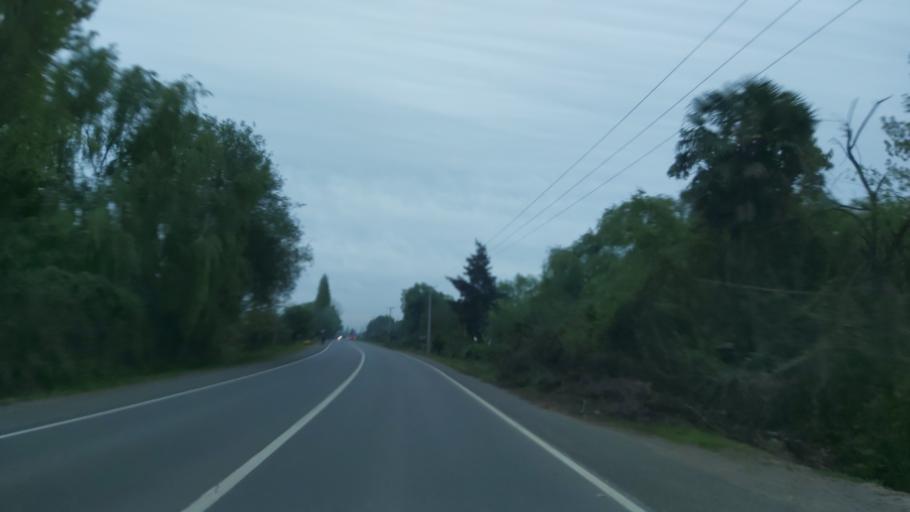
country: CL
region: Maule
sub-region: Provincia de Linares
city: Linares
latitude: -35.7613
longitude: -71.5080
